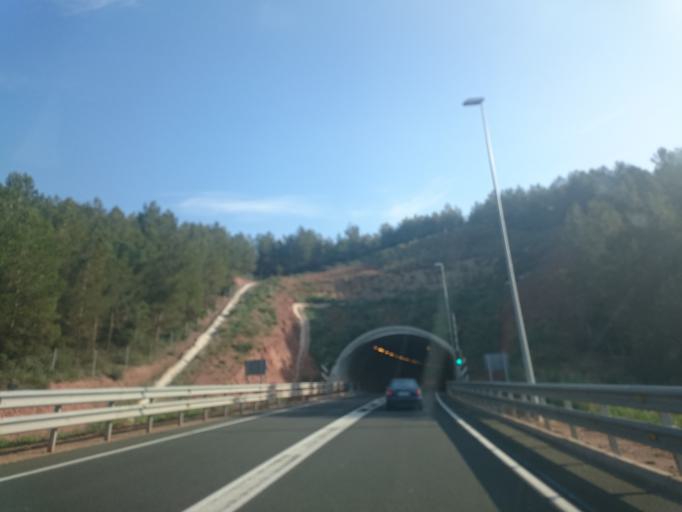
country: ES
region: Catalonia
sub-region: Provincia de Barcelona
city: Sant Salvador de Guardiola
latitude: 41.7048
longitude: 1.7797
